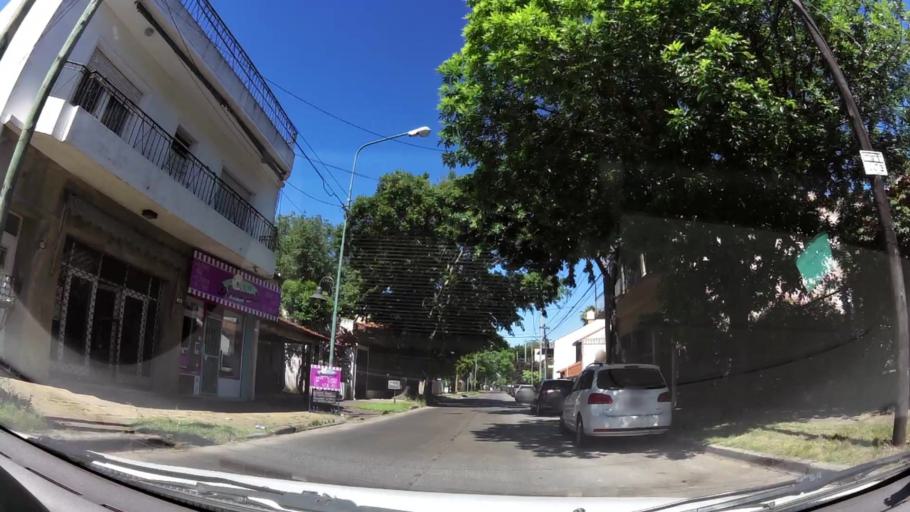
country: AR
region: Buenos Aires
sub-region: Partido de Vicente Lopez
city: Olivos
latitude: -34.5219
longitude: -58.5002
